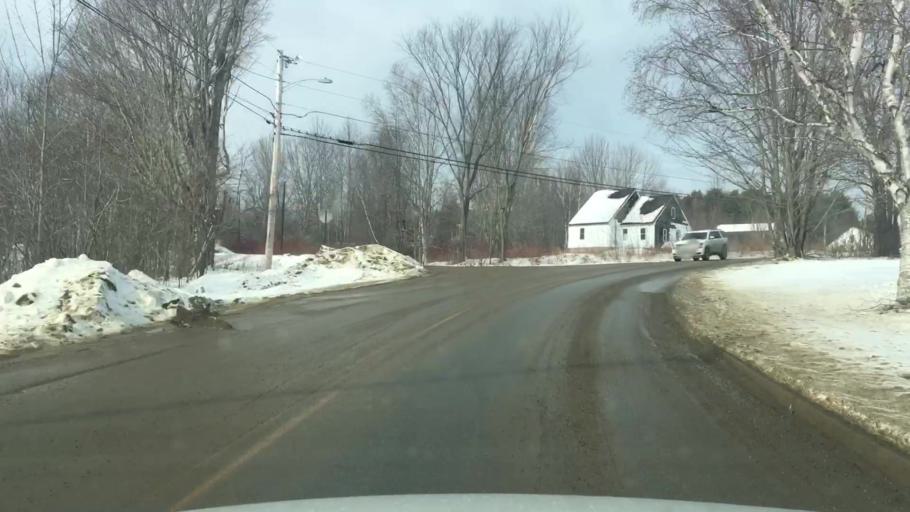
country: US
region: Maine
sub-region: Penobscot County
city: Hermon
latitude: 44.7682
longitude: -68.9600
